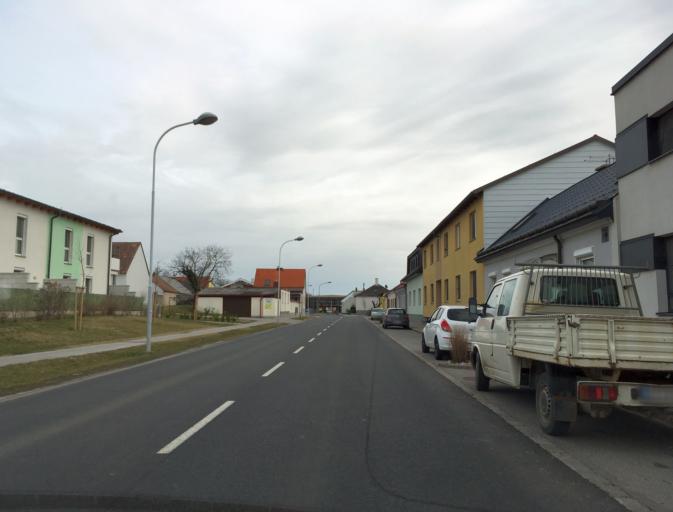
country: AT
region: Lower Austria
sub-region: Politischer Bezirk Ganserndorf
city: Lassee
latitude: 48.2210
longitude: 16.8134
